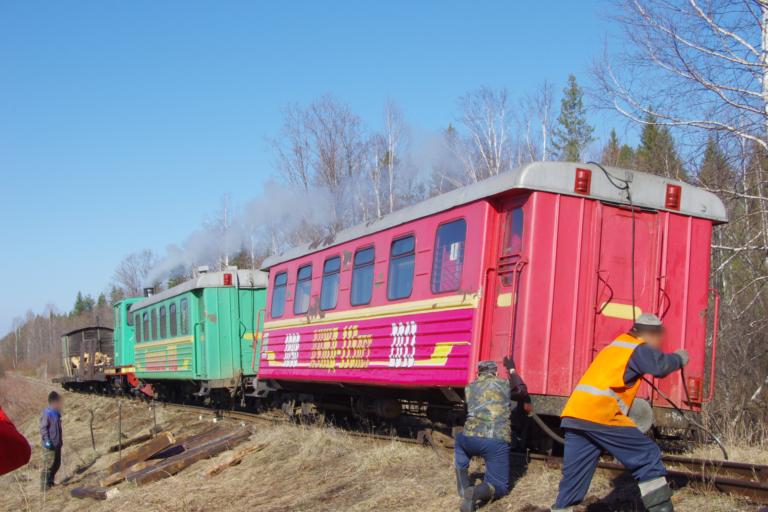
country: RU
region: Sverdlovsk
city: Verkhnyaya Sinyachikha
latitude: 58.2458
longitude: 62.1305
